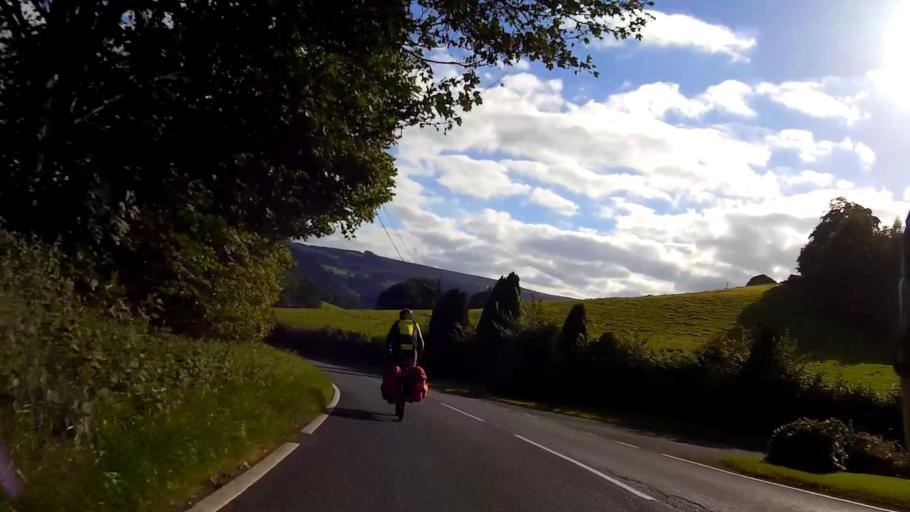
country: GB
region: Wales
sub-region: Denbighshire
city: Llangollen
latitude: 52.9994
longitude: -3.1931
